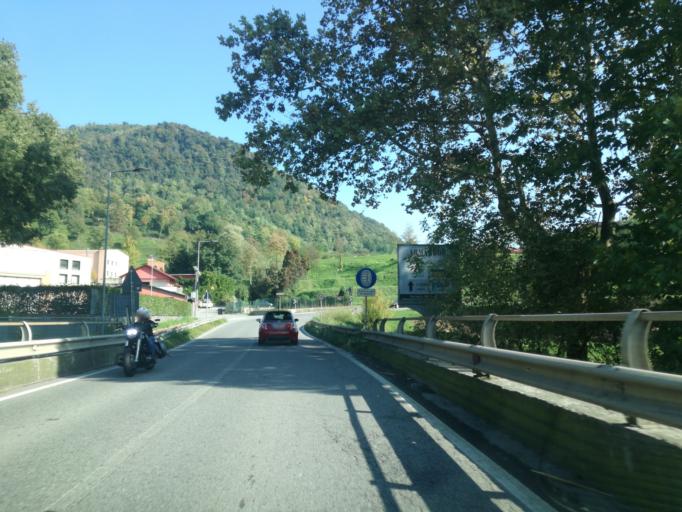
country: IT
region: Lombardy
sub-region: Provincia di Bergamo
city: Caprino
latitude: 45.7385
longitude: 9.4855
